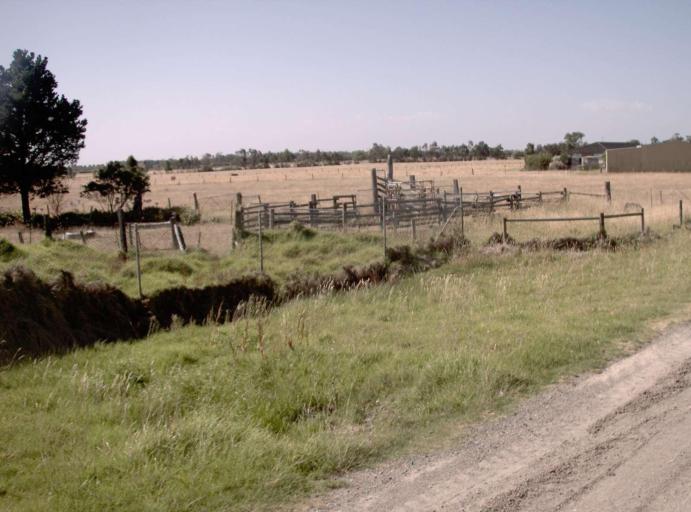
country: AU
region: Victoria
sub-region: Frankston
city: Carrum Downs
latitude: -38.0845
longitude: 145.1843
